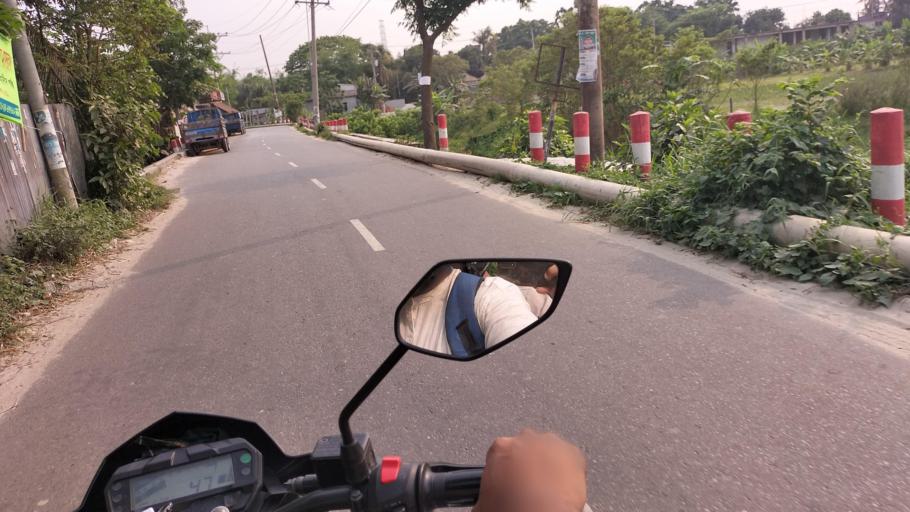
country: BD
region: Dhaka
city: Azimpur
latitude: 23.6676
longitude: 90.3413
